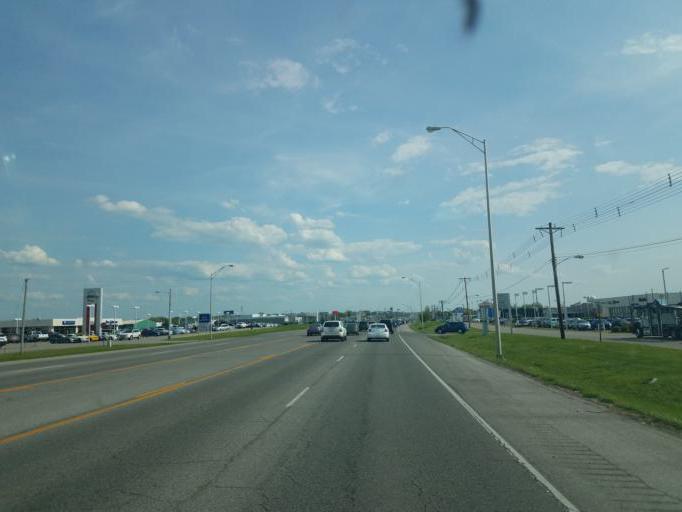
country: US
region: Kentucky
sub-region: Warren County
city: Bowling Green
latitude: 36.9585
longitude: -86.4288
